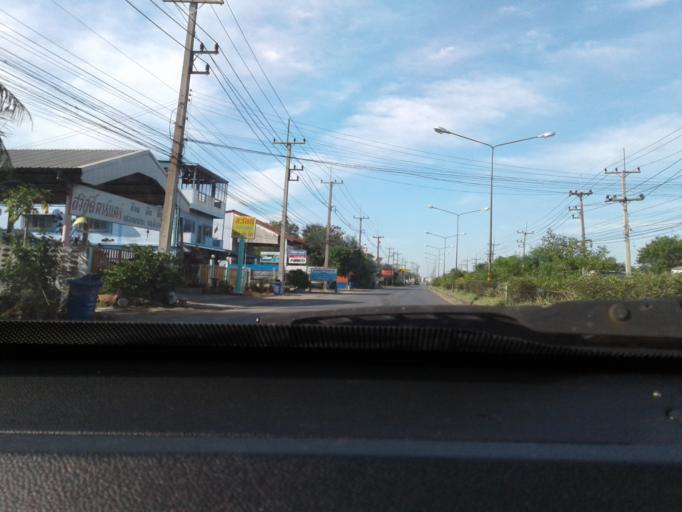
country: TH
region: Nakhon Pathom
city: Salaya
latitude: 13.8661
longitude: 100.2955
